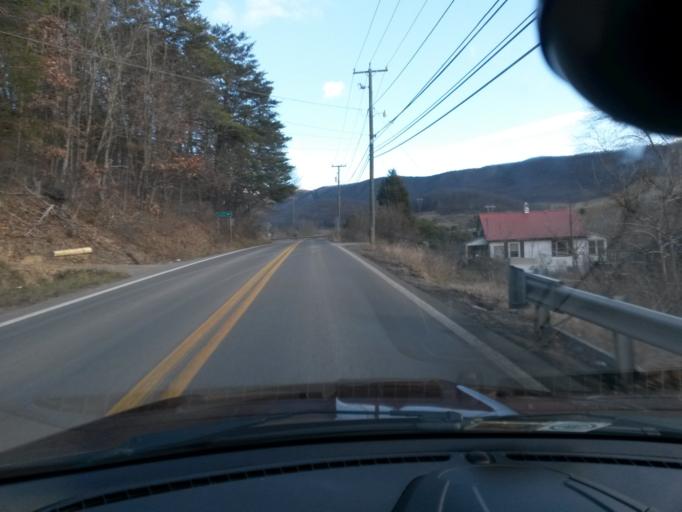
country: US
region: Virginia
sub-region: Giles County
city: Narrows
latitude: 37.3958
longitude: -80.7894
